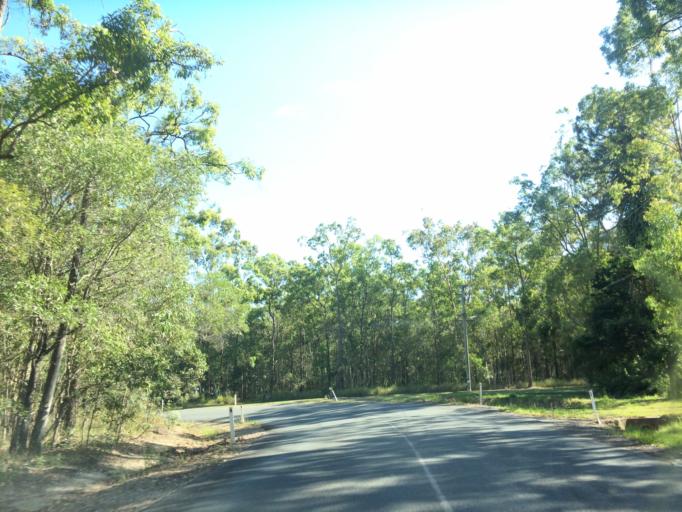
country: AU
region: Queensland
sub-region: Ipswich
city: Springfield Lakes
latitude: -27.7123
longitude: 152.9603
